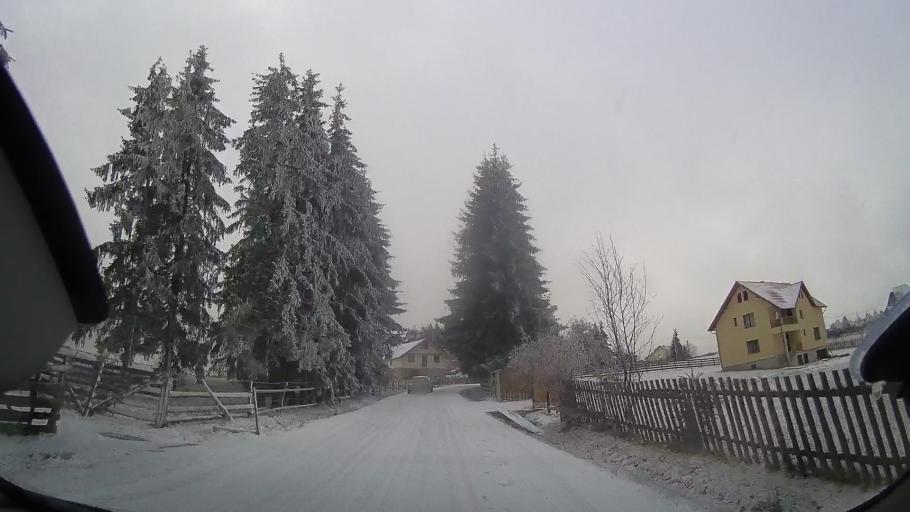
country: RO
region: Cluj
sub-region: Comuna Marisel
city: Marisel
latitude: 46.6622
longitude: 23.1217
